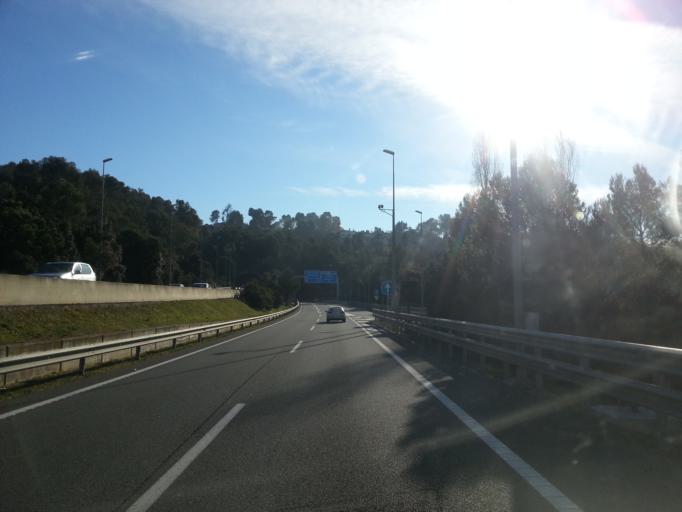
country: ES
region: Catalonia
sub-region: Provincia de Barcelona
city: Sant Cugat del Valles
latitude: 41.4472
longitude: 2.0692
